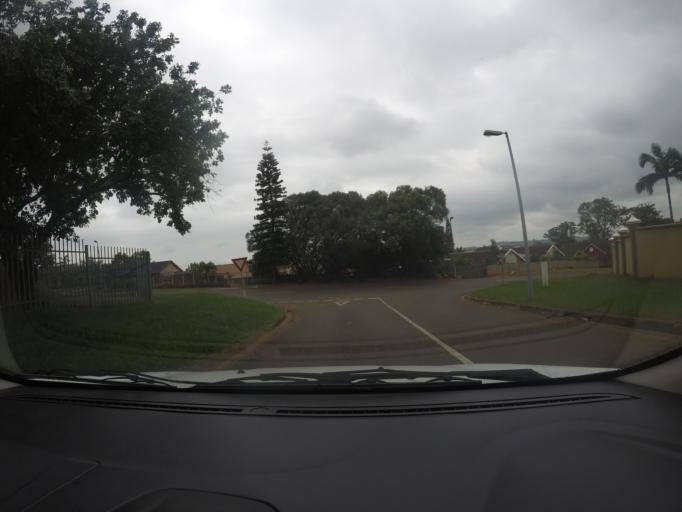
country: ZA
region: KwaZulu-Natal
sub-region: uThungulu District Municipality
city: Empangeni
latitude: -28.7690
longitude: 31.8962
